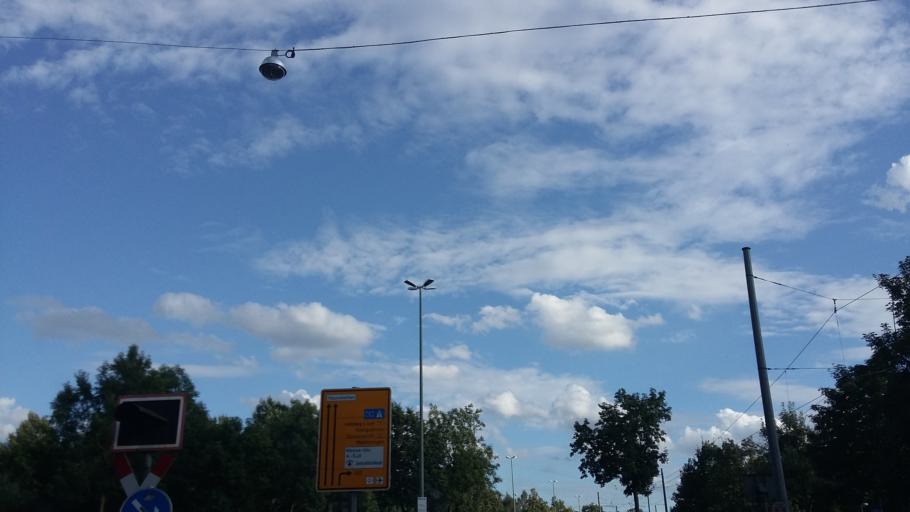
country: DE
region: Bavaria
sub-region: Swabia
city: Augsburg
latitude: 48.3388
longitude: 10.9073
